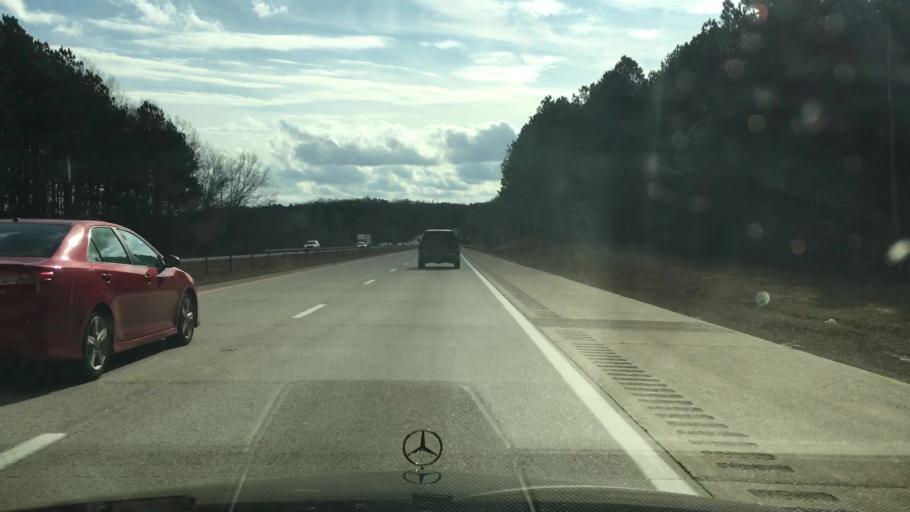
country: US
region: North Carolina
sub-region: Johnston County
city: Clayton
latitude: 35.5685
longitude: -78.5763
